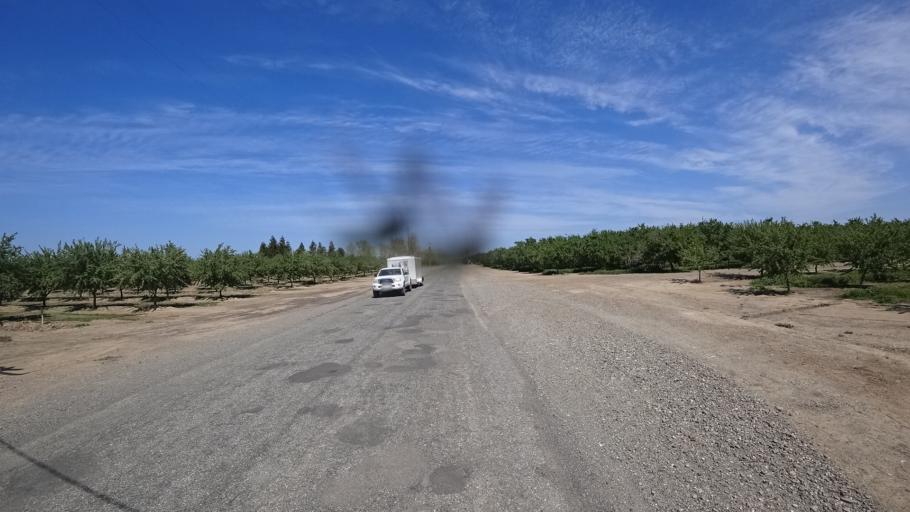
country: US
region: California
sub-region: Glenn County
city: Hamilton City
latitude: 39.6485
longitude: -122.0742
